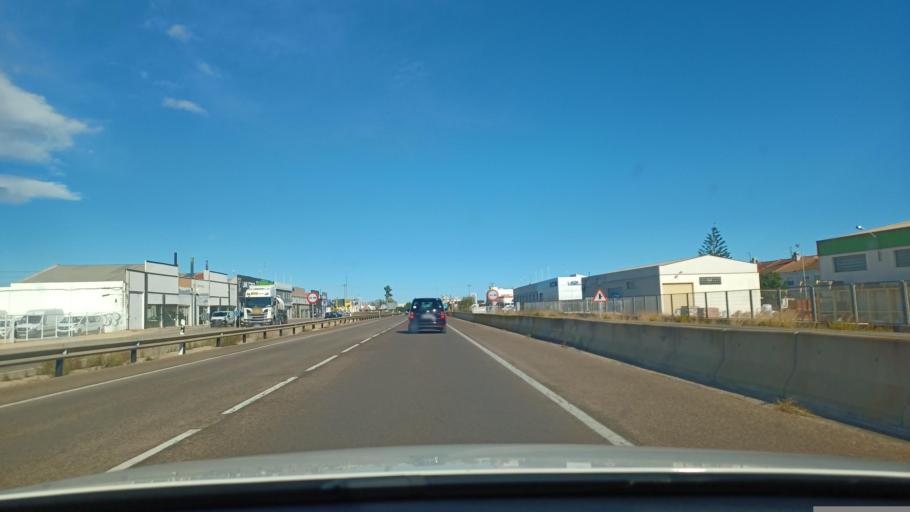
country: ES
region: Valencia
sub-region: Provincia de Castello
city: Vinaros
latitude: 40.4776
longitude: 0.4696
